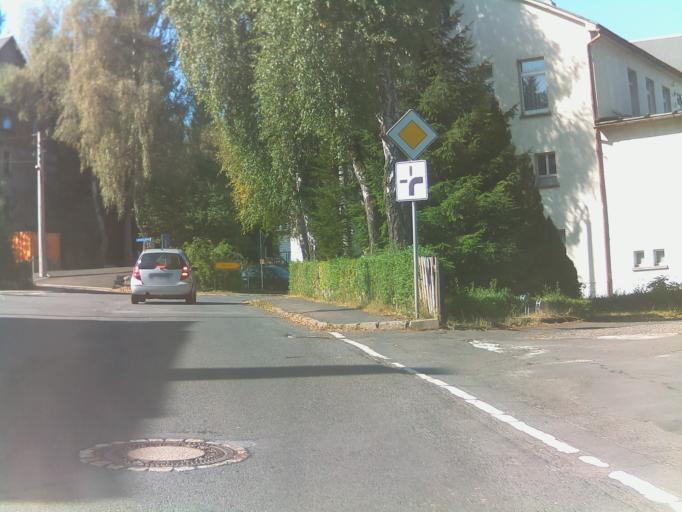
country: DE
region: Thuringia
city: Schmiedefeld am Rennsteig
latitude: 50.6075
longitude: 10.8132
